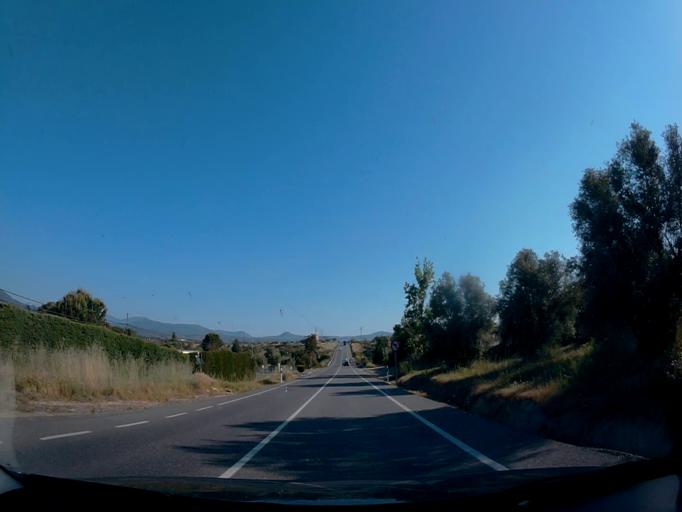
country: ES
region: Castille-La Mancha
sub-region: Province of Toledo
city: Escalona
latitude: 40.1410
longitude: -4.4037
